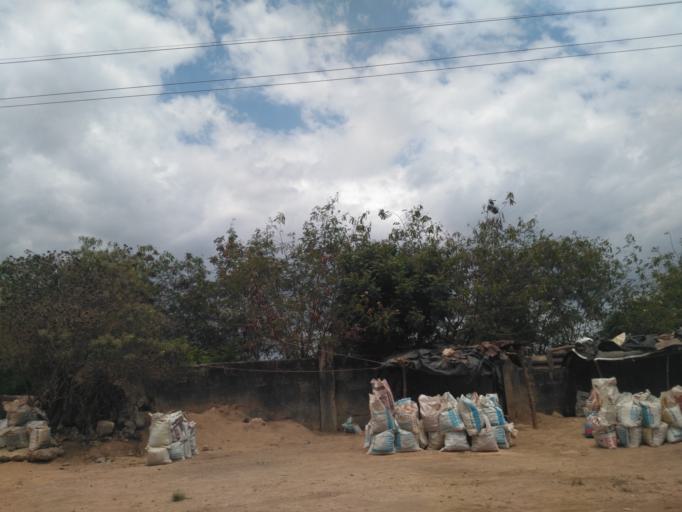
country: TZ
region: Dar es Salaam
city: Magomeni
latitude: -6.7634
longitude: 39.2726
